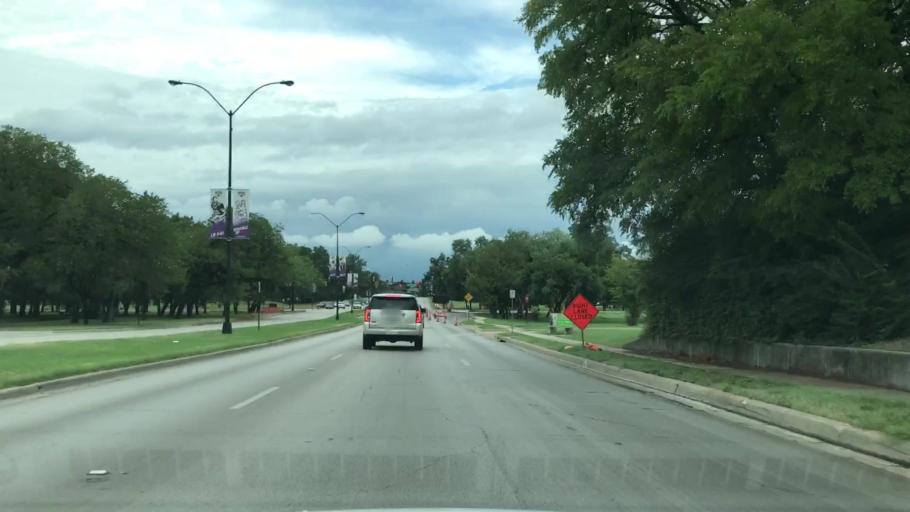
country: US
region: Texas
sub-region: Tarrant County
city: Fort Worth
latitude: 32.7201
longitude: -97.3612
